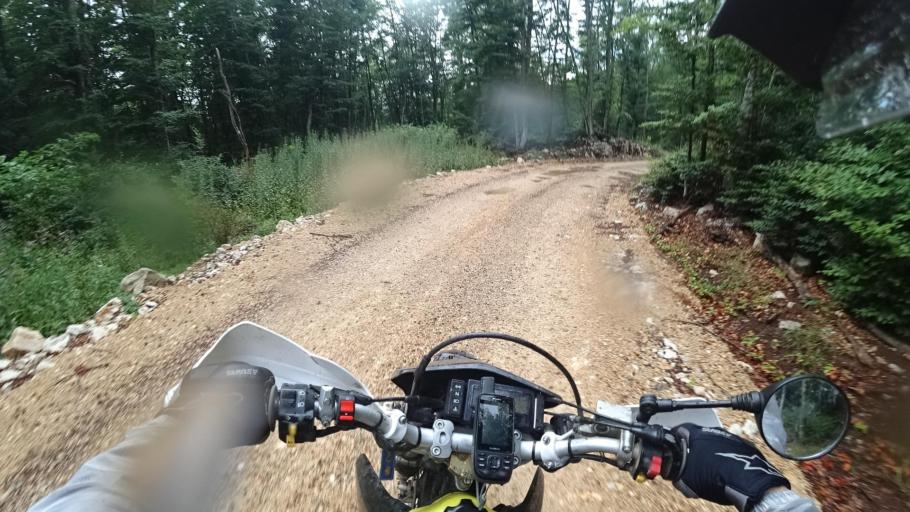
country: HR
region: Licko-Senjska
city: Jezerce
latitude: 44.7105
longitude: 15.6592
